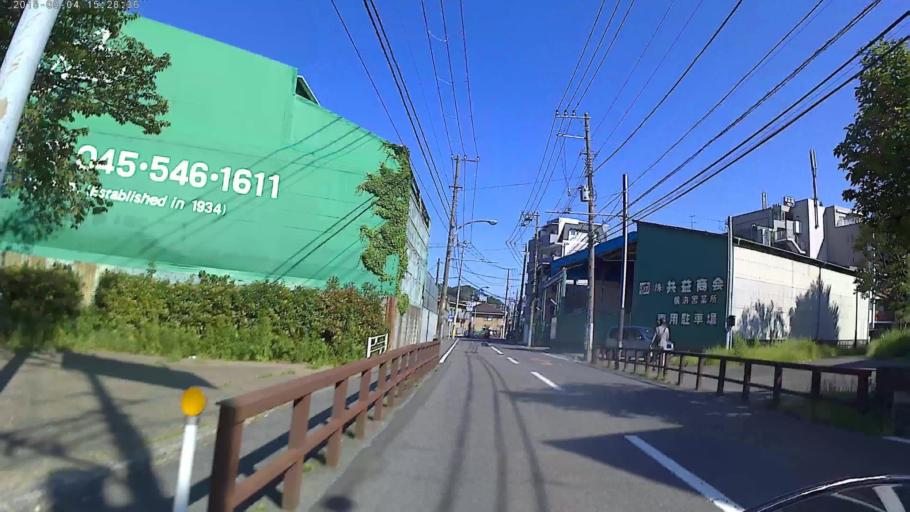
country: JP
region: Kanagawa
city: Yokohama
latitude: 35.5279
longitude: 139.6206
